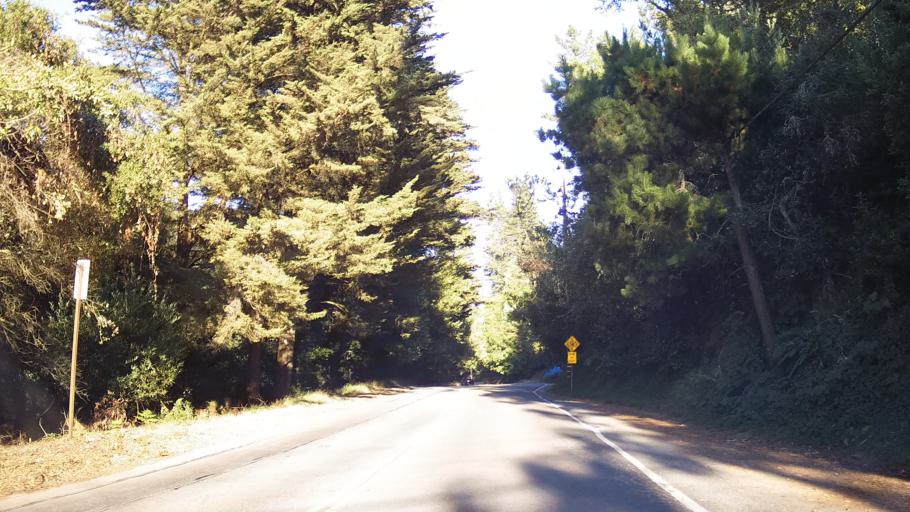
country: US
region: California
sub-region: Contra Costa County
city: Orinda
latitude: 37.8477
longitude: -122.2003
